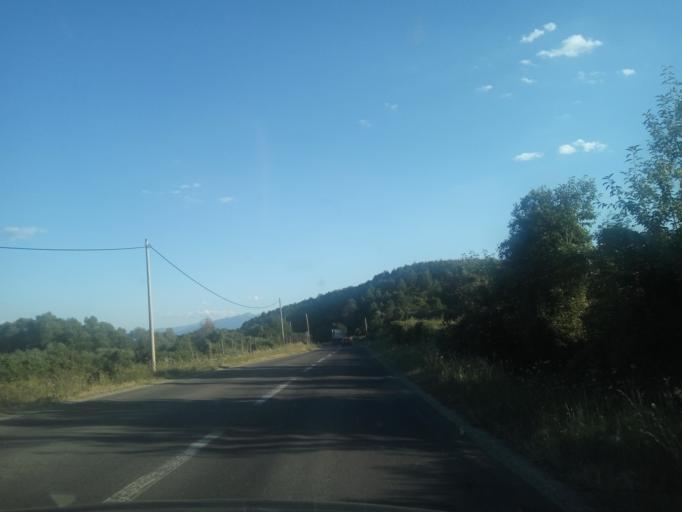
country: XK
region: Pec
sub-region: Komuna e Pejes
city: Kosuriq
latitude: 42.4688
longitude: 20.5046
